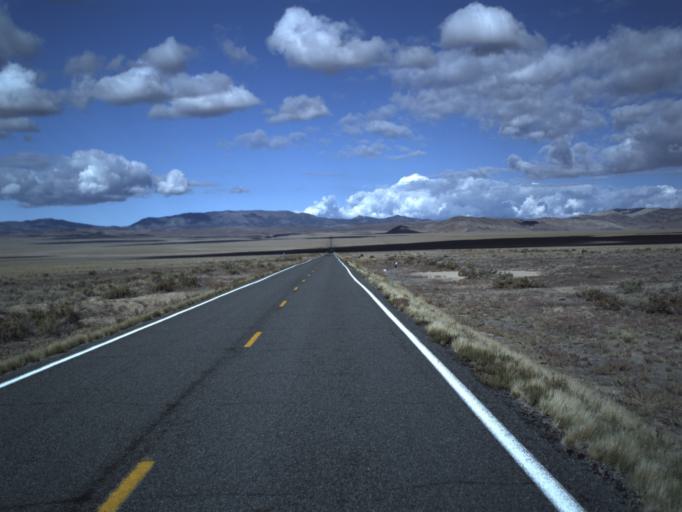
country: US
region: Utah
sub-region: Beaver County
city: Milford
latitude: 38.5431
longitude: -113.7109
